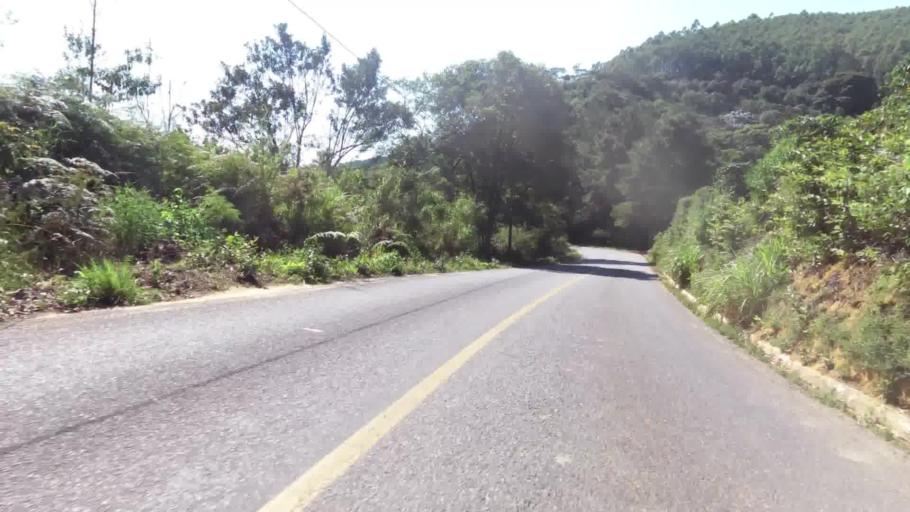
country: BR
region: Espirito Santo
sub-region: Marechal Floriano
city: Marechal Floriano
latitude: -20.4351
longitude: -40.8803
